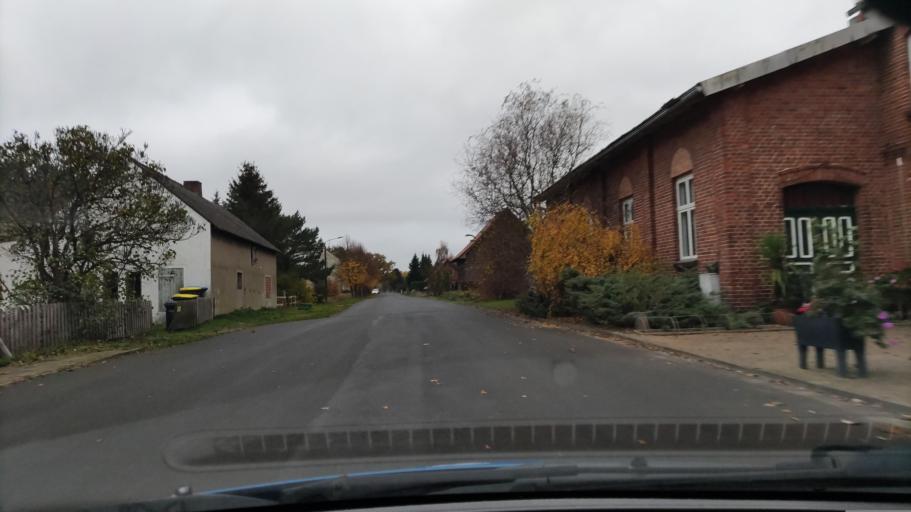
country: DE
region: Mecklenburg-Vorpommern
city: Domitz
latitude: 53.1719
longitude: 11.2289
